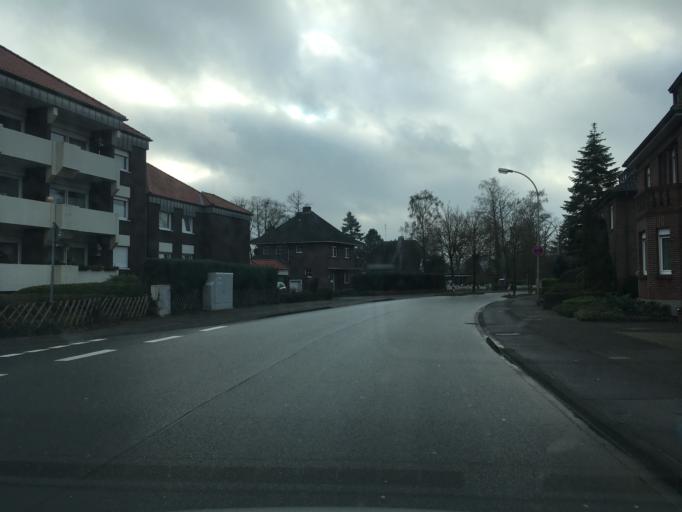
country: DE
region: North Rhine-Westphalia
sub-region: Regierungsbezirk Munster
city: Gronau
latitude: 52.2090
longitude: 7.0175
